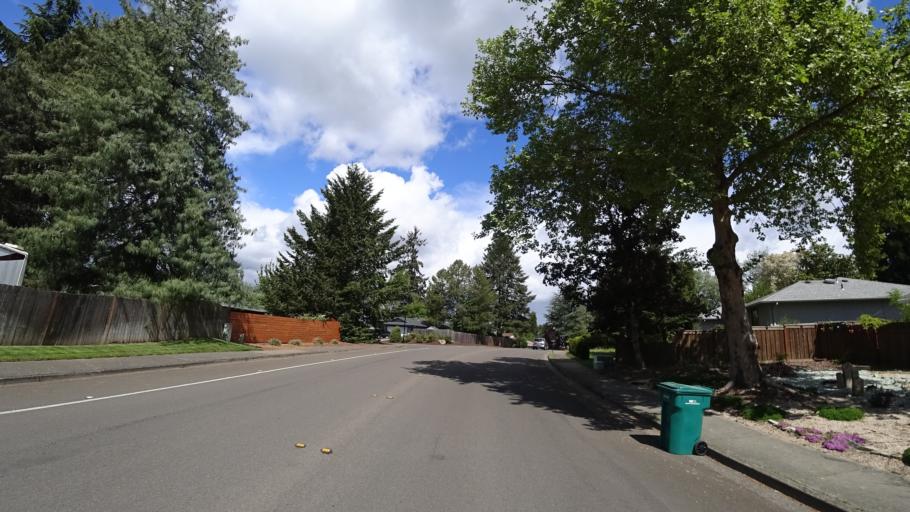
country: US
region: Oregon
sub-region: Washington County
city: Aloha
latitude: 45.4788
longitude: -122.8416
